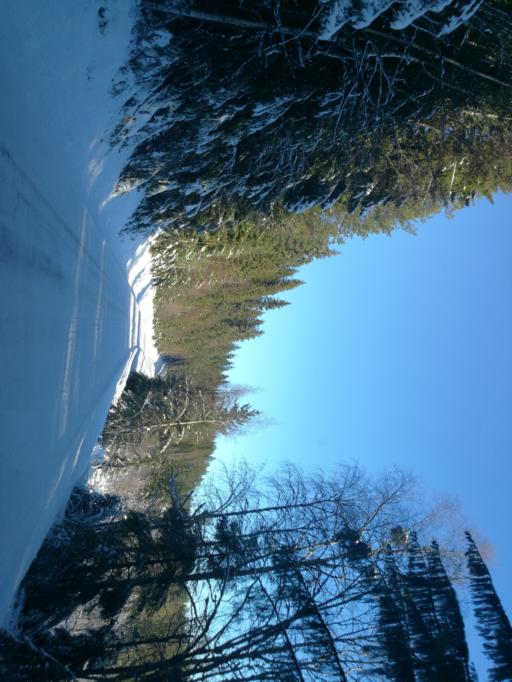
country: SE
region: Vaermland
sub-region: Torsby Kommun
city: Torsby
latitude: 60.5634
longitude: 12.6310
